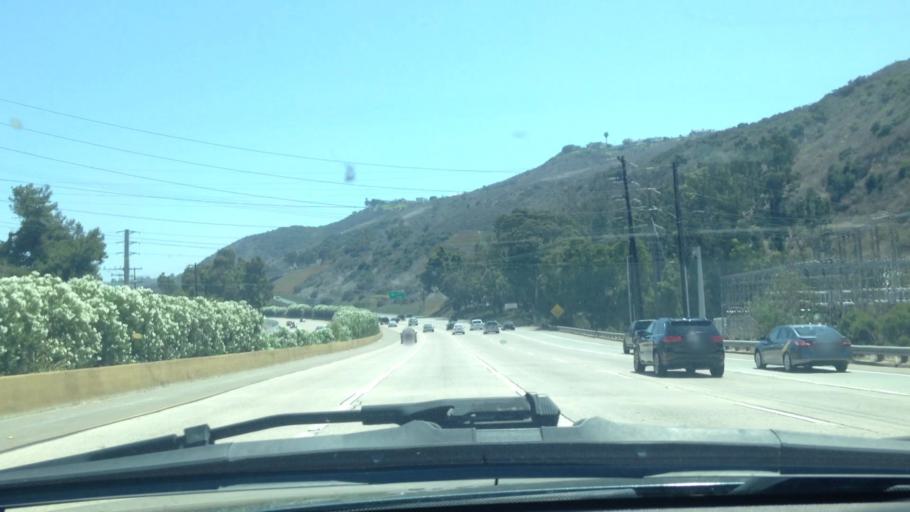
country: US
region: California
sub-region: San Diego County
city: La Jolla
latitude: 32.8454
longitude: -117.2364
